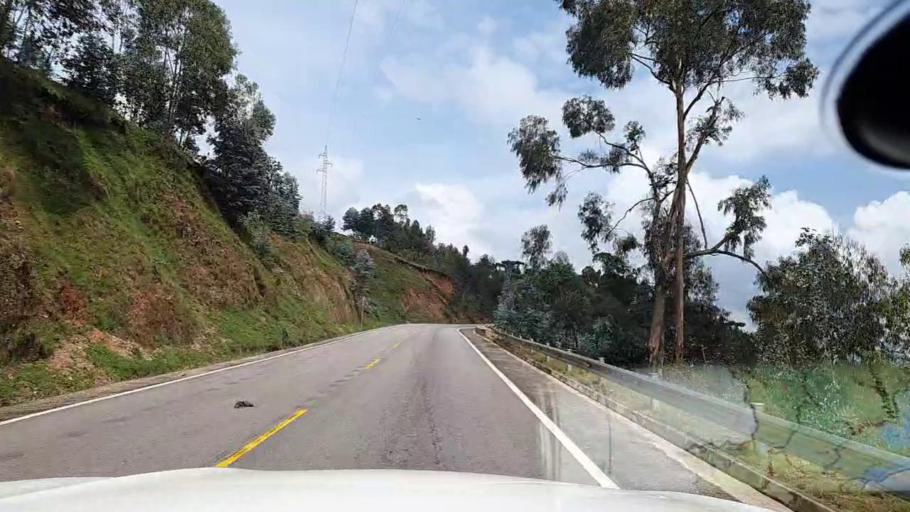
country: RW
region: Southern Province
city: Nzega
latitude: -2.5068
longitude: 29.4991
